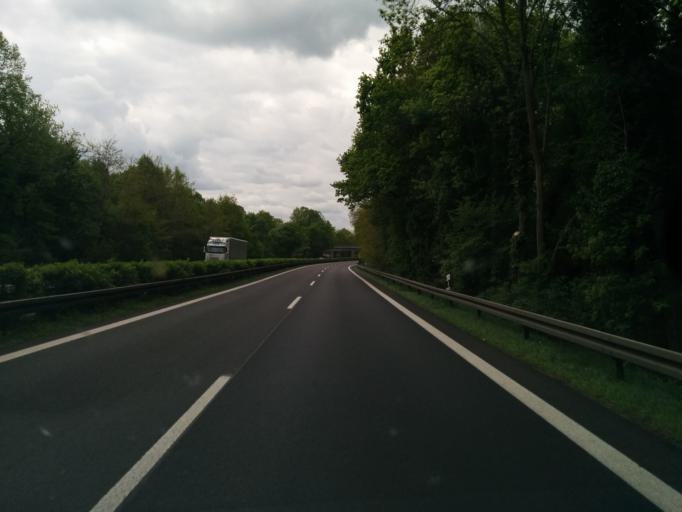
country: DE
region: Brandenburg
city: Werder
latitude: 52.4031
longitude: 12.8707
